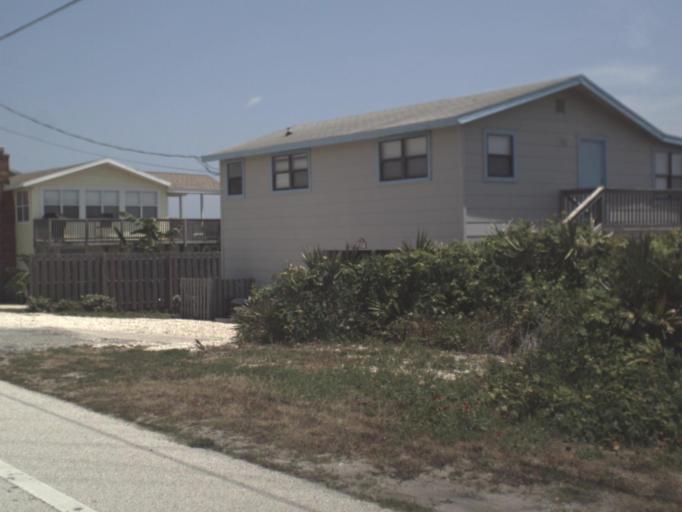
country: US
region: Florida
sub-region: Saint Johns County
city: Villano Beach
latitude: 30.0124
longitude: -81.3207
